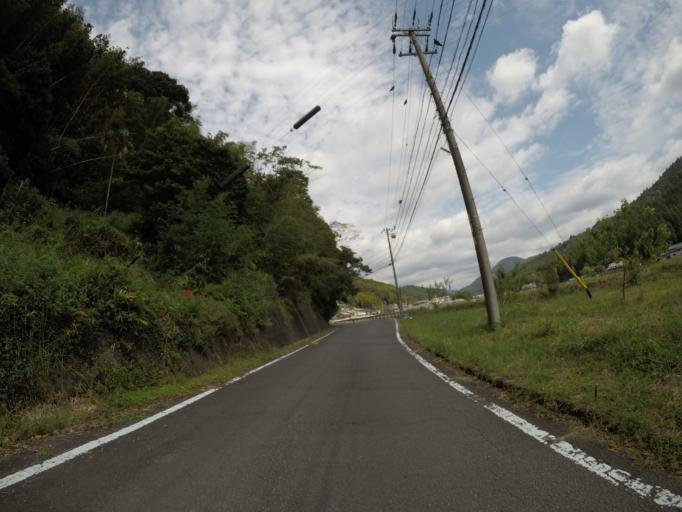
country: JP
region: Shizuoka
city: Kanaya
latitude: 34.8694
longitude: 138.1322
